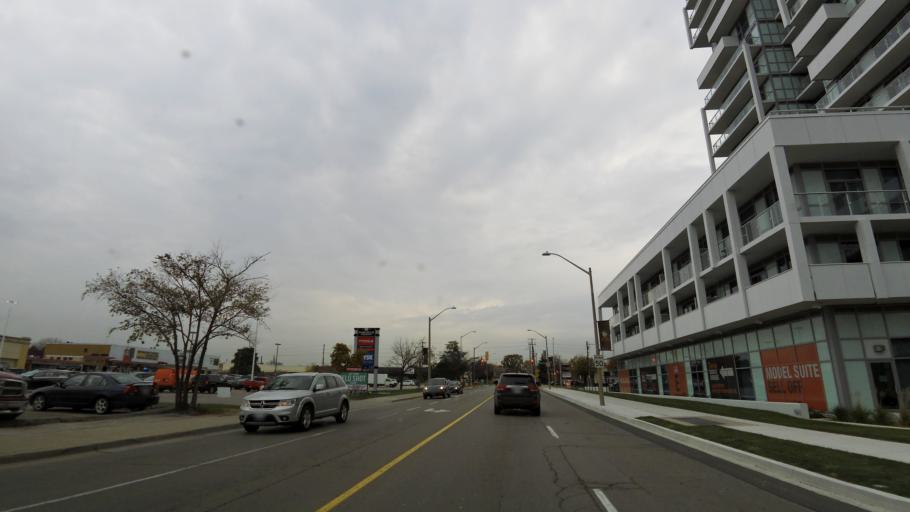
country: CA
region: Ontario
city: Oakville
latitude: 43.4470
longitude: -79.6875
